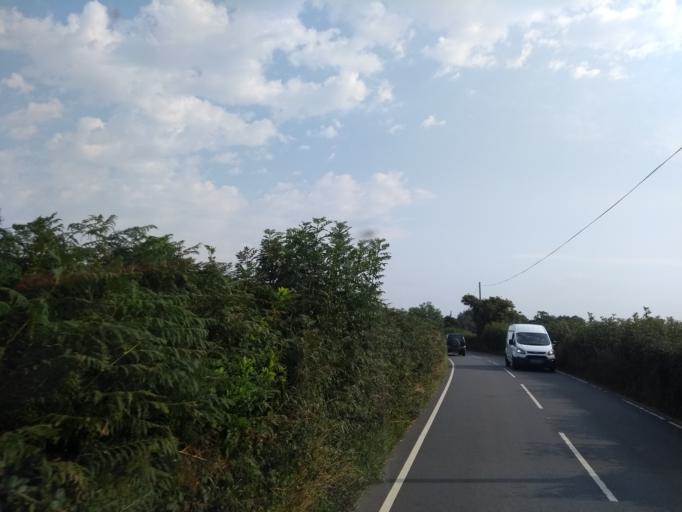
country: GB
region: England
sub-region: Devon
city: Axminster
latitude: 50.7613
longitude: -3.0150
